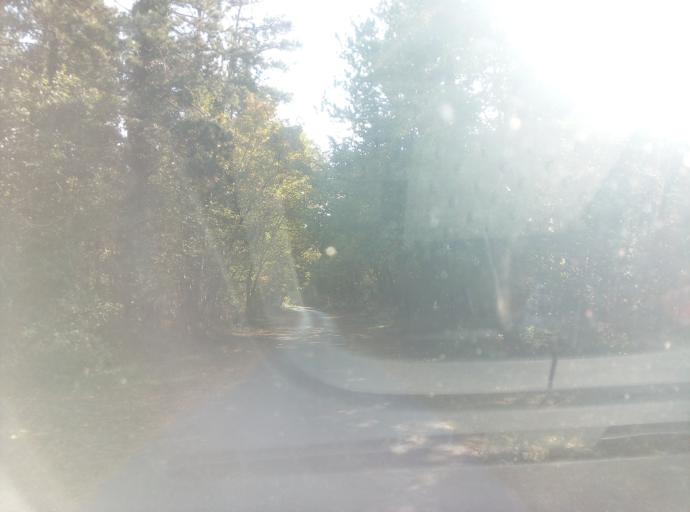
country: SI
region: Ajdovscina
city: Lokavec
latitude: 45.8198
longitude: 13.8520
